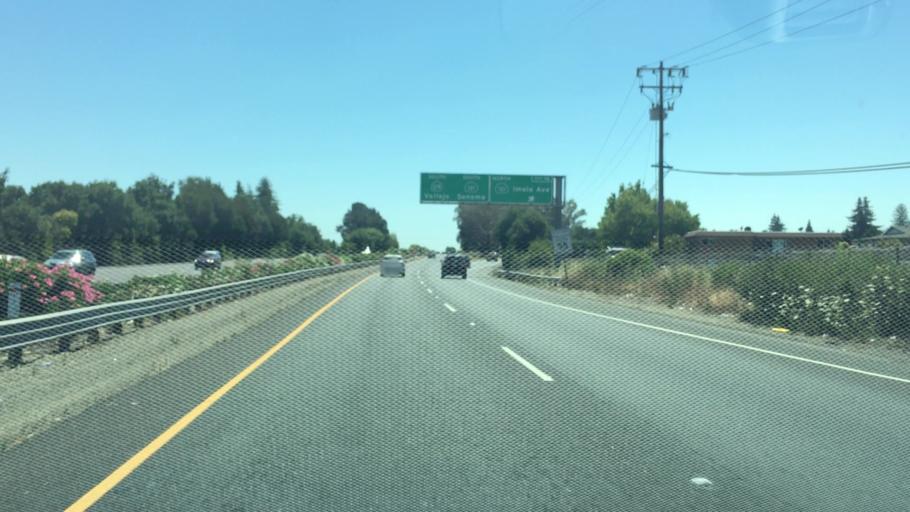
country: US
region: California
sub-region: Napa County
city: Napa
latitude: 38.2858
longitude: -122.3008
